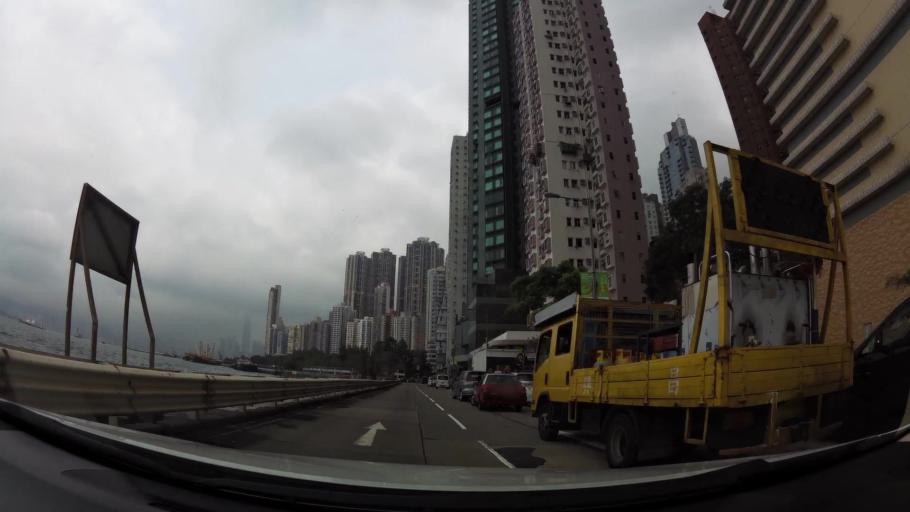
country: HK
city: Hong Kong
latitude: 22.2838
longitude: 114.1262
